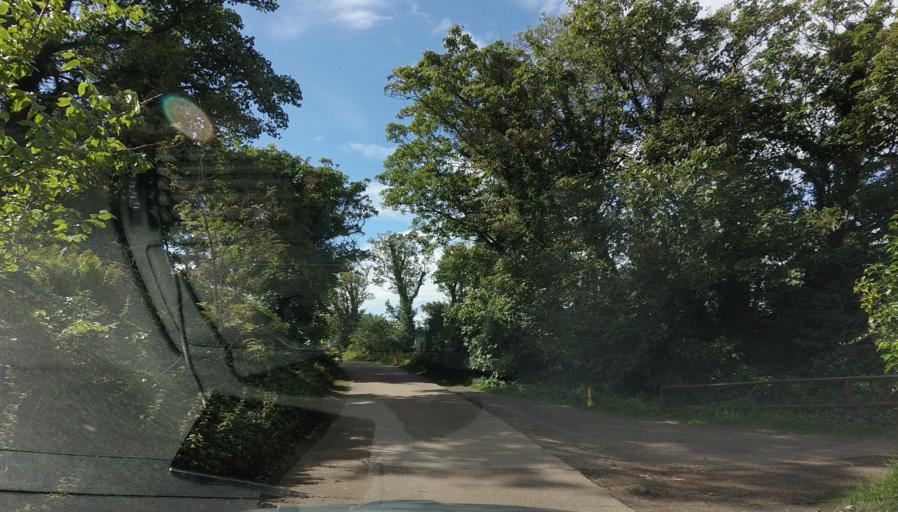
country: GB
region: Scotland
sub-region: East Lothian
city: East Linton
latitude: 56.0517
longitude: -2.6424
